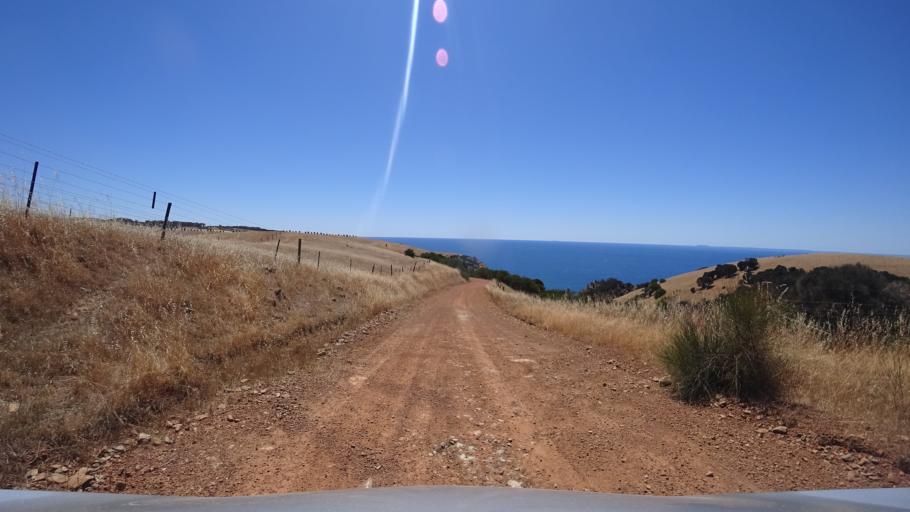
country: AU
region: South Australia
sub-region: Kangaroo Island
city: Kingscote
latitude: -35.6786
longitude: 136.9766
